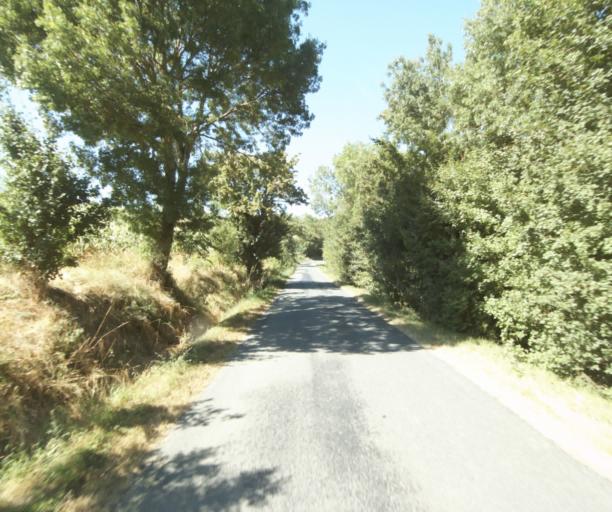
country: FR
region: Midi-Pyrenees
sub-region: Departement de la Haute-Garonne
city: Auriac-sur-Vendinelle
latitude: 43.5227
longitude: 1.8850
